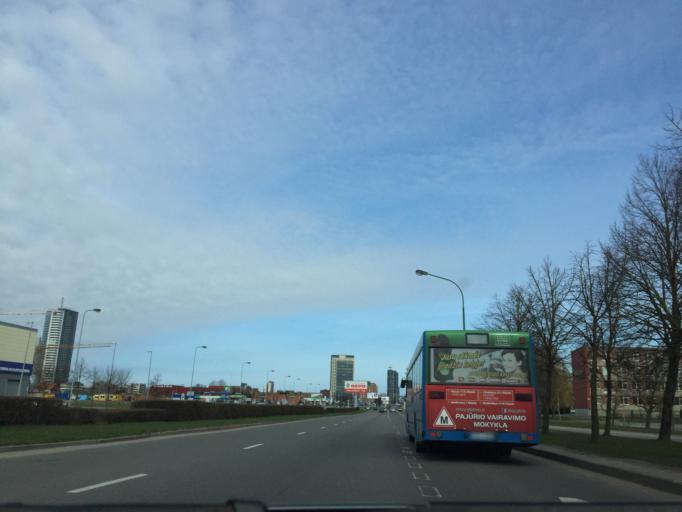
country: LT
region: Klaipedos apskritis
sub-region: Klaipeda
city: Klaipeda
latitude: 55.6873
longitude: 21.1582
